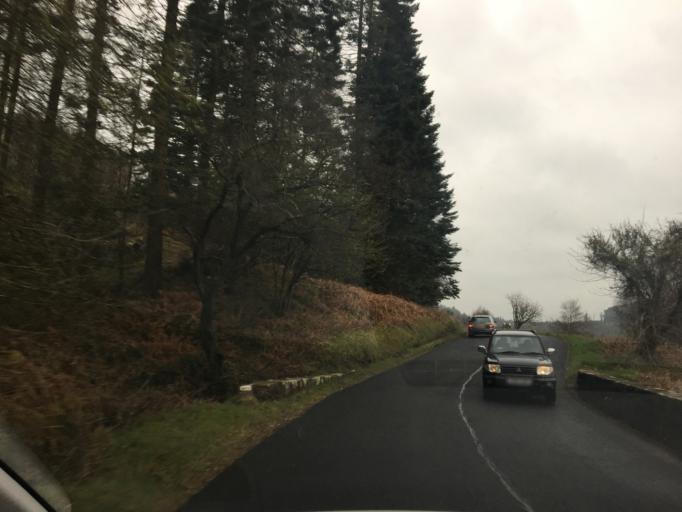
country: GB
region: Scotland
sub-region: North Ayrshire
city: Lamlash
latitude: 55.5455
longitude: -5.1334
